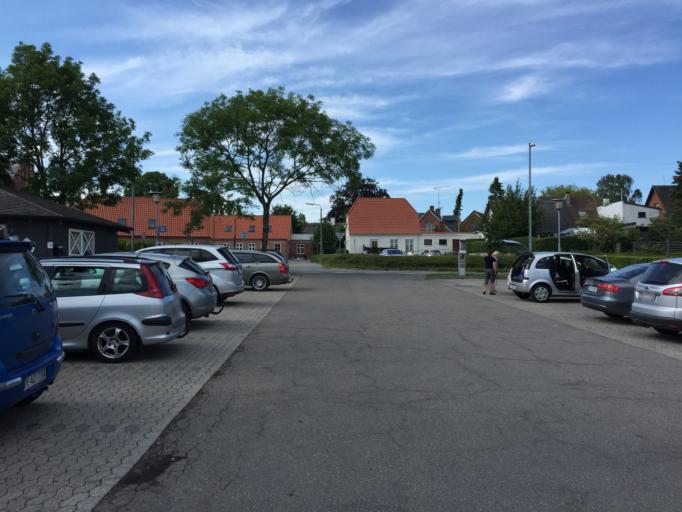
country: DK
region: Capital Region
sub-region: Gribskov Kommune
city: Helsinge
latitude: 56.0227
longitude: 12.1990
